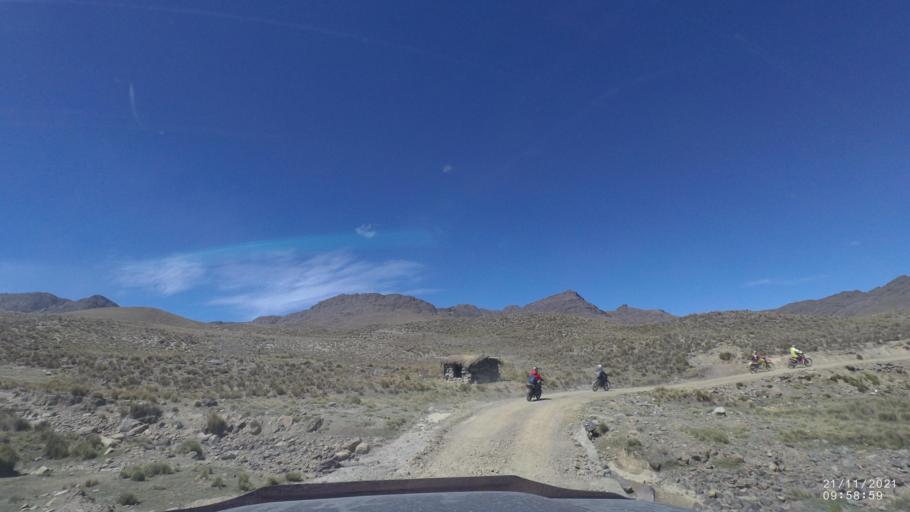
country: BO
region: Cochabamba
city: Cochabamba
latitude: -17.0356
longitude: -66.2785
